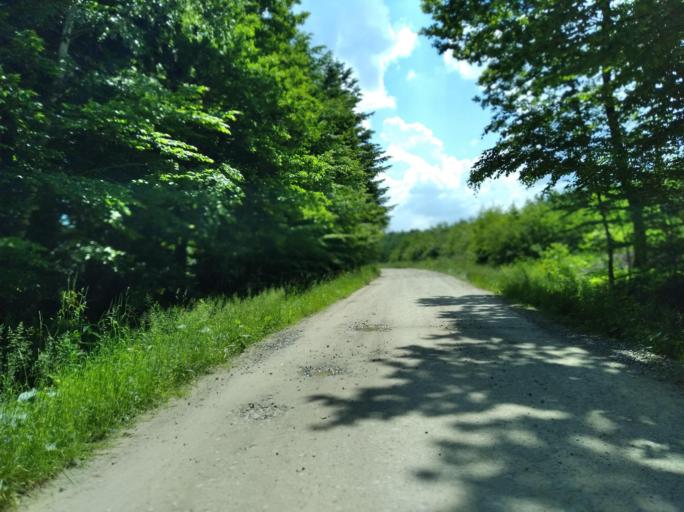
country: PL
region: Subcarpathian Voivodeship
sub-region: Powiat ropczycko-sedziszowski
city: Zagorzyce
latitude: 49.9723
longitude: 21.6870
